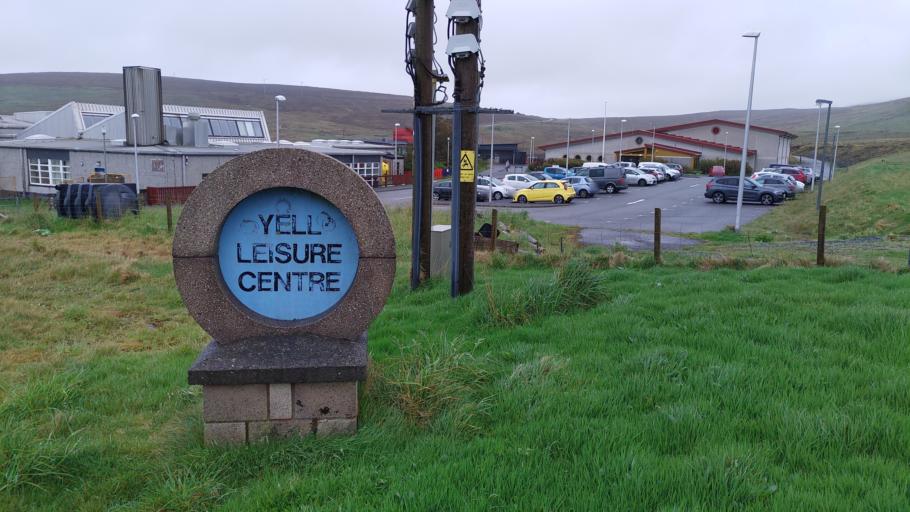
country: GB
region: Scotland
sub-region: Shetland Islands
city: Shetland
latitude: 60.5979
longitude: -1.0660
